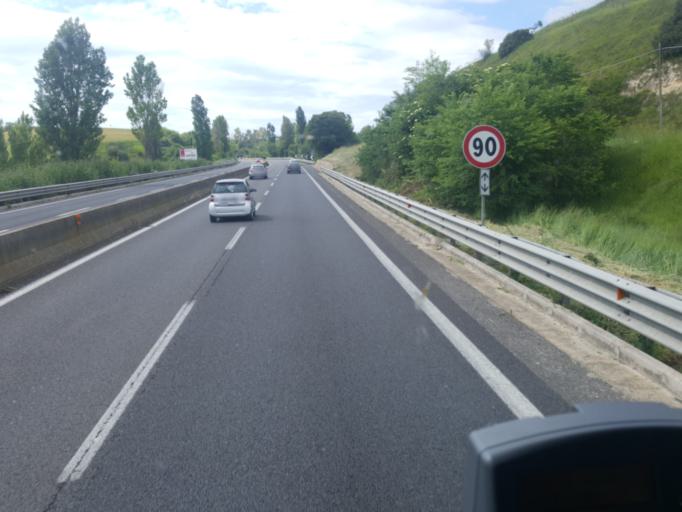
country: IT
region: Latium
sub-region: Citta metropolitana di Roma Capitale
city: Valle Santa
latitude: 41.8931
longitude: 12.2941
